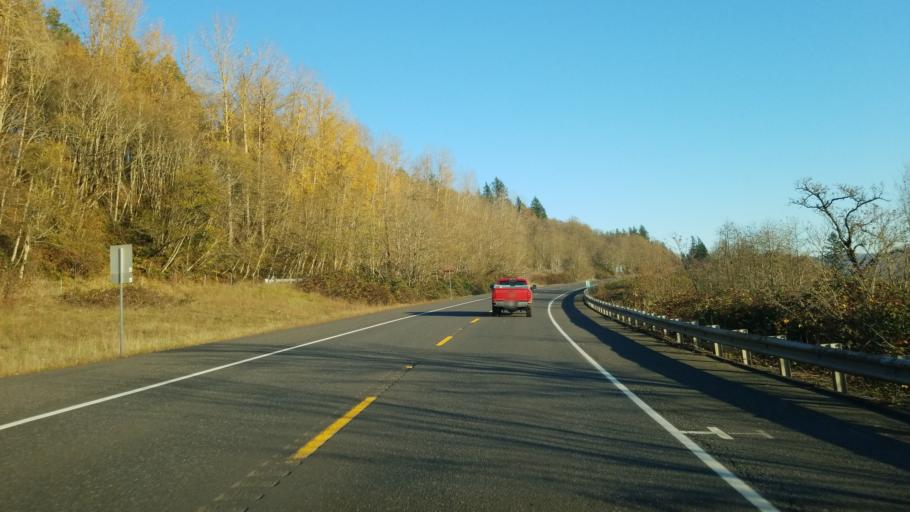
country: US
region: Washington
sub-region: Clark County
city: Washougal
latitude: 45.5715
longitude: -122.2985
